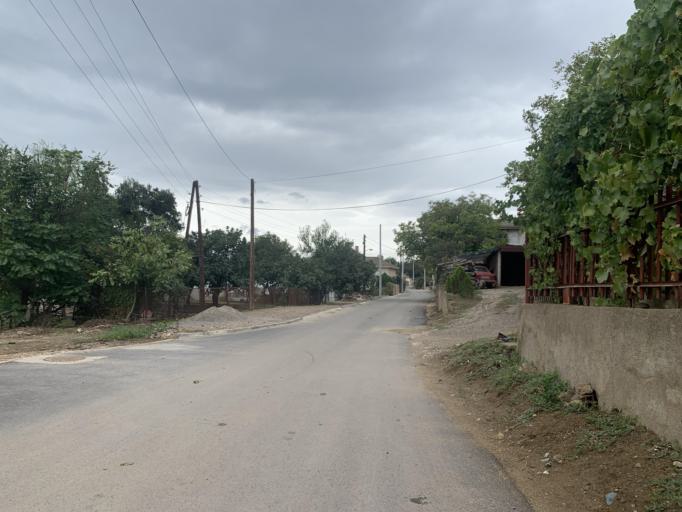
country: MK
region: Bogdanci
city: Bogdanci
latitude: 41.1914
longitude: 22.5389
